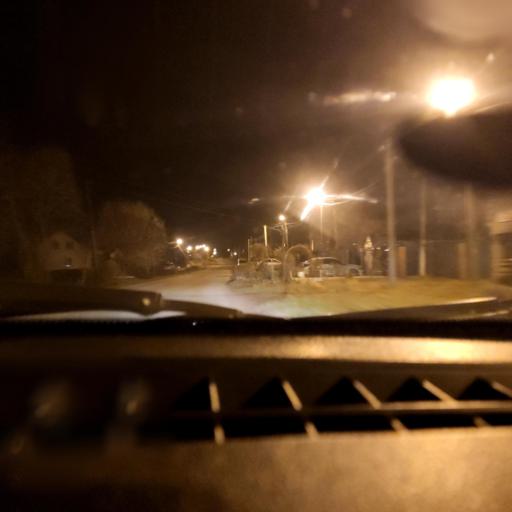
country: RU
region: Bashkortostan
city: Kabakovo
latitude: 54.6373
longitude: 56.0789
